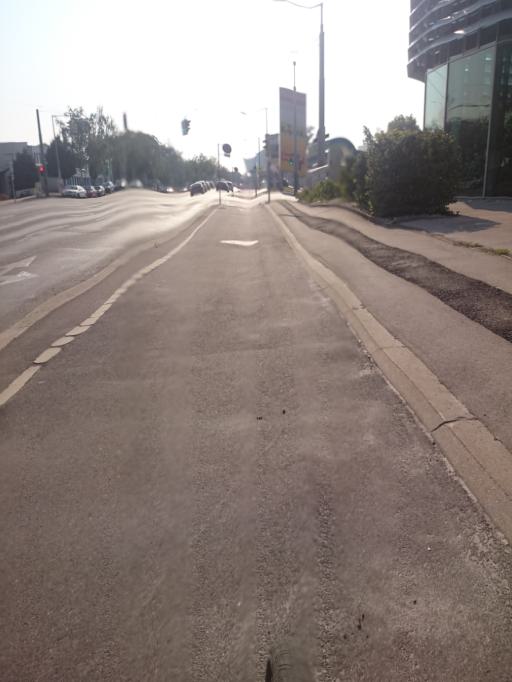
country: AT
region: Lower Austria
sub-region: Politischer Bezirk Wien-Umgebung
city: Gerasdorf bei Wien
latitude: 48.2709
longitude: 16.4110
